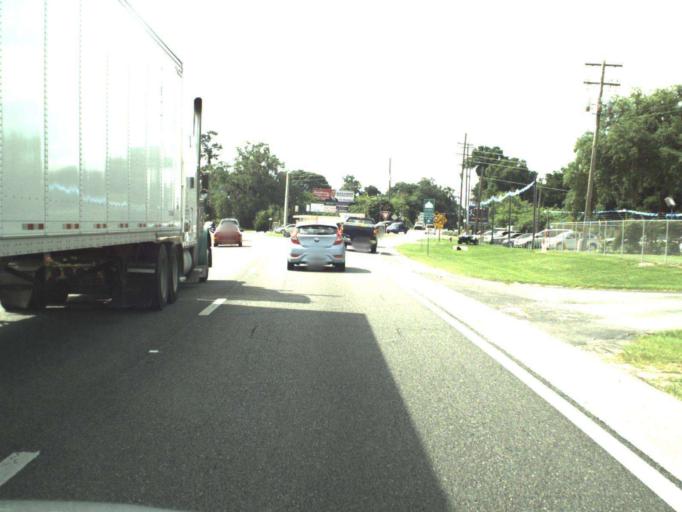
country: US
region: Florida
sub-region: Marion County
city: Ocala
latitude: 29.1465
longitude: -82.1142
